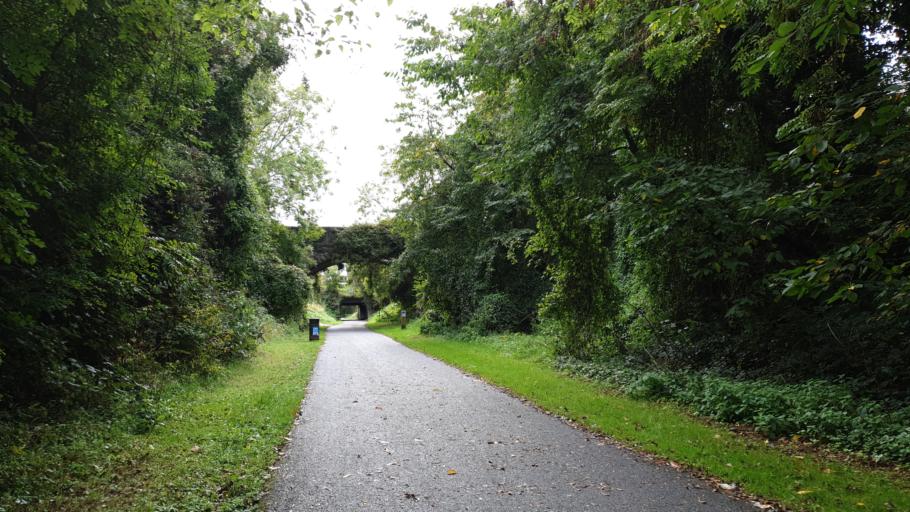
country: IE
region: Munster
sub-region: County Cork
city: Cork
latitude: 51.8912
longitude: -8.4128
